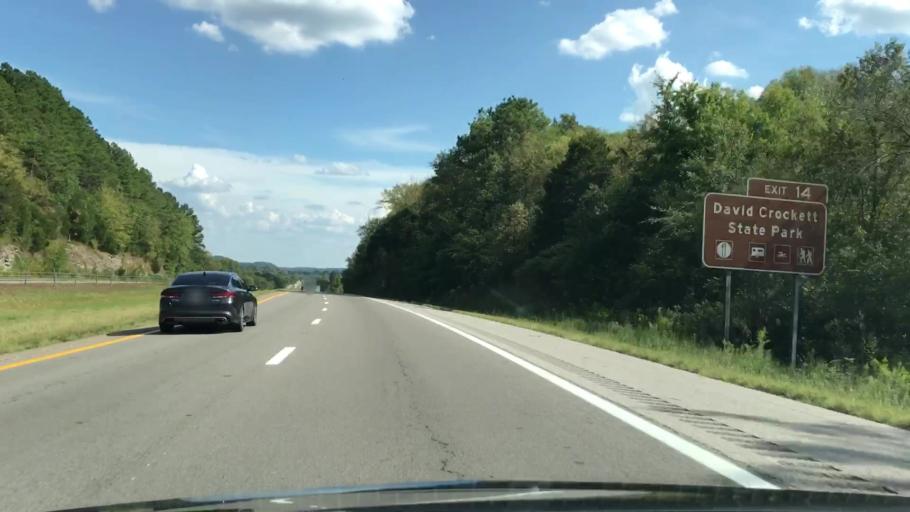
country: US
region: Tennessee
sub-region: Giles County
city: Pulaski
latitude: 35.2187
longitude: -86.8876
